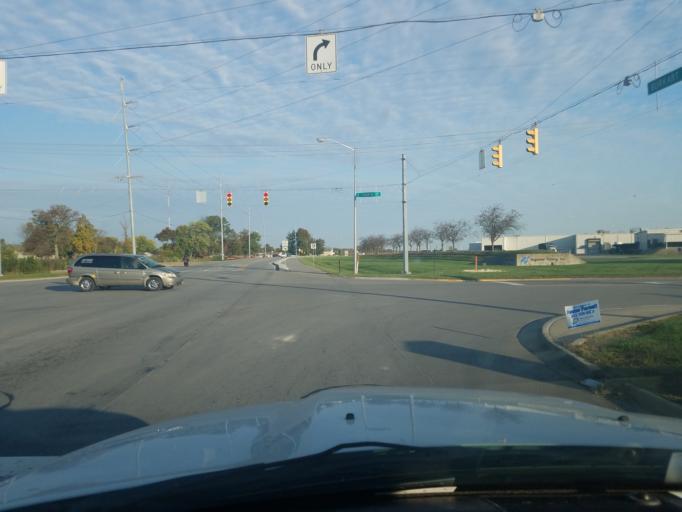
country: US
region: Indiana
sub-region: Jackson County
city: Seymour
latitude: 38.9653
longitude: -85.8697
